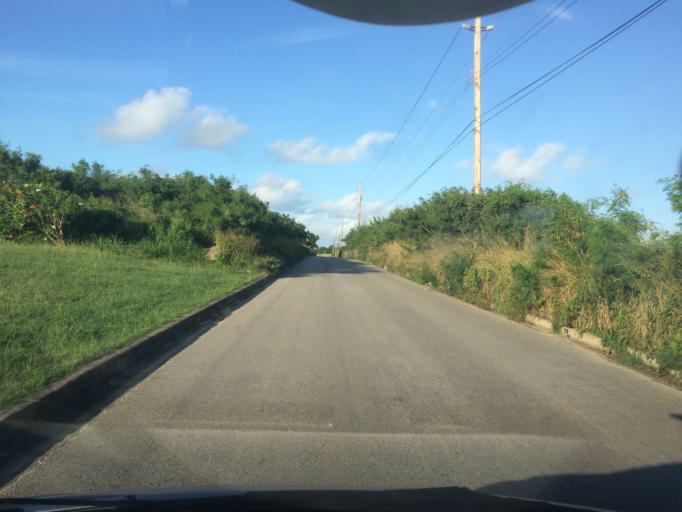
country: BB
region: Saint Lucy
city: Checker Hall
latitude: 13.3054
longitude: -59.6400
